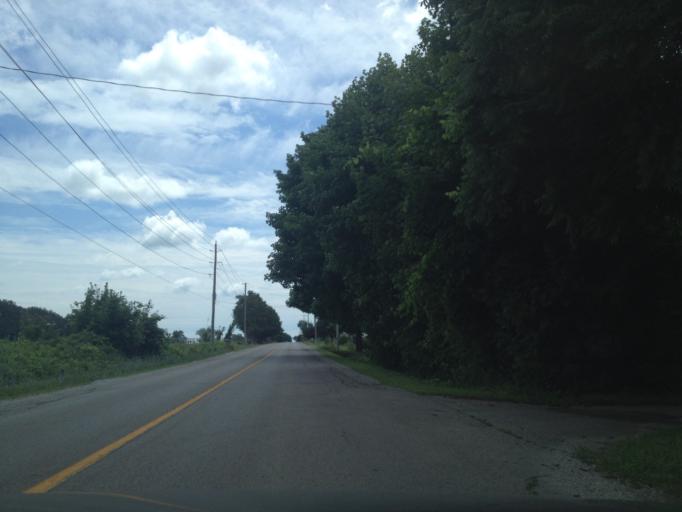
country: CA
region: Ontario
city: Norfolk County
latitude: 42.8242
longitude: -80.3316
